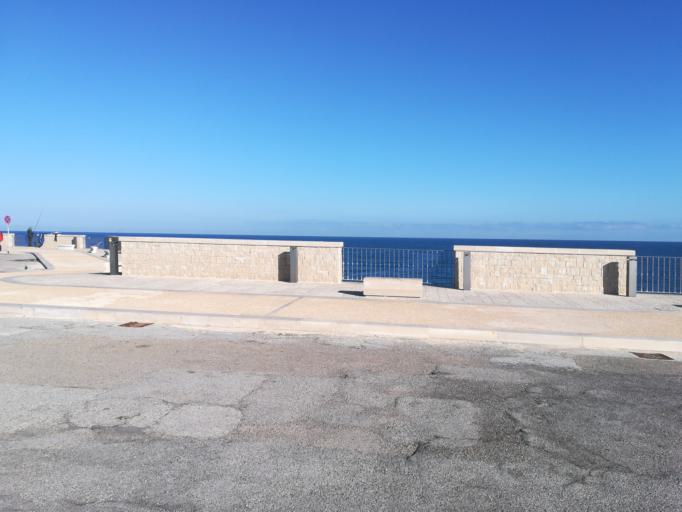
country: IT
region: Apulia
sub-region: Provincia di Bari
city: Polignano a Mare
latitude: 40.9965
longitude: 17.2243
